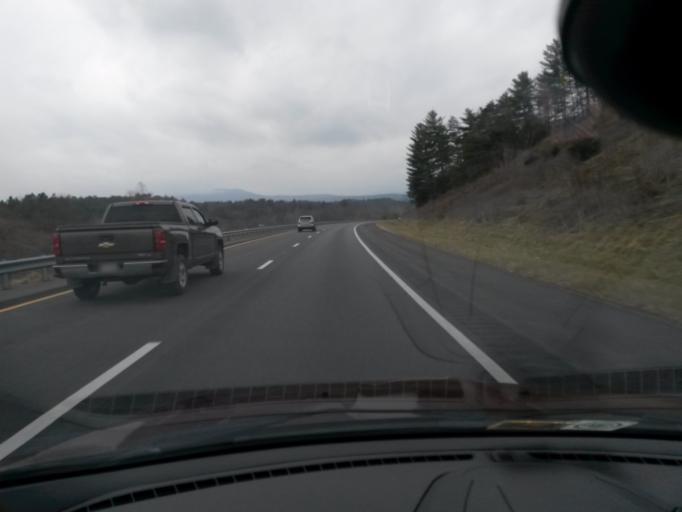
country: US
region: Virginia
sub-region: Alleghany County
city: Clifton Forge
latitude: 37.7957
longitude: -79.7217
